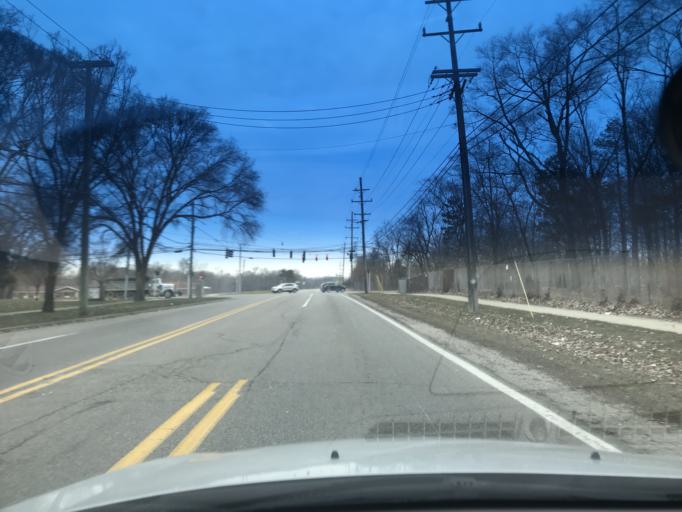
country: US
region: Michigan
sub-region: Macomb County
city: Shelby
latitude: 42.6549
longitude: -83.0490
